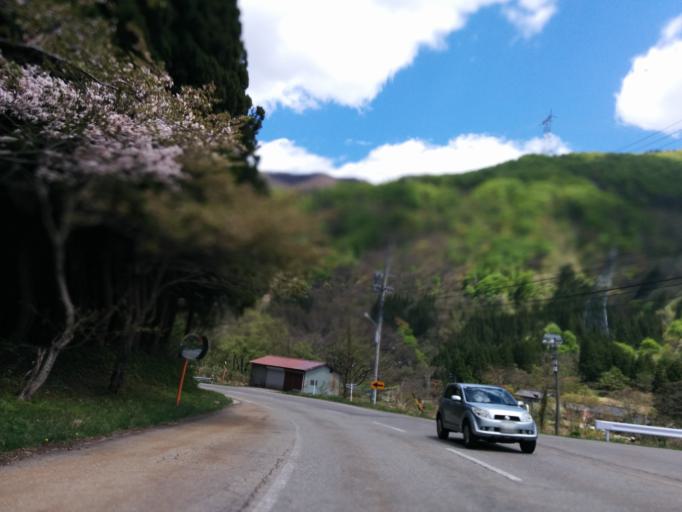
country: JP
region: Toyama
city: Fukumitsu
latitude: 36.3152
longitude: 136.8992
